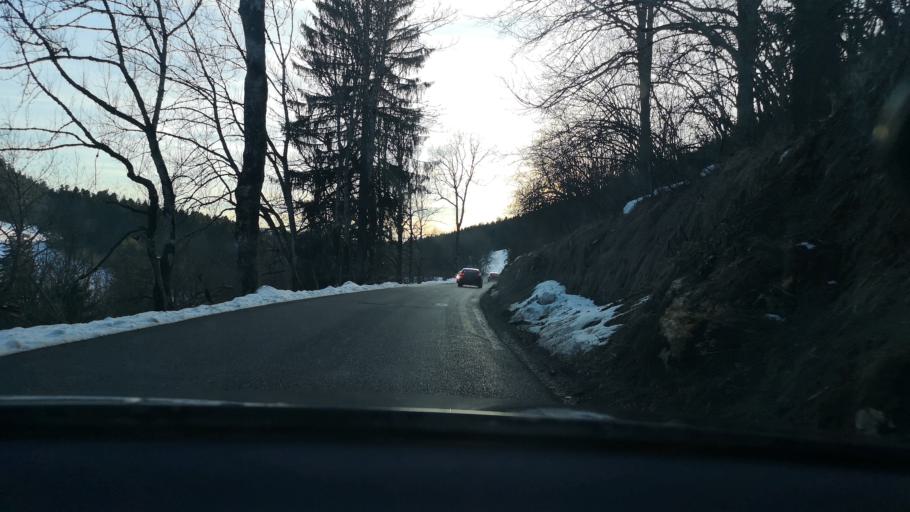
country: FR
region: Franche-Comte
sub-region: Departement du Doubs
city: La Cluse-et-Mijoux
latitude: 46.9227
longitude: 6.3968
